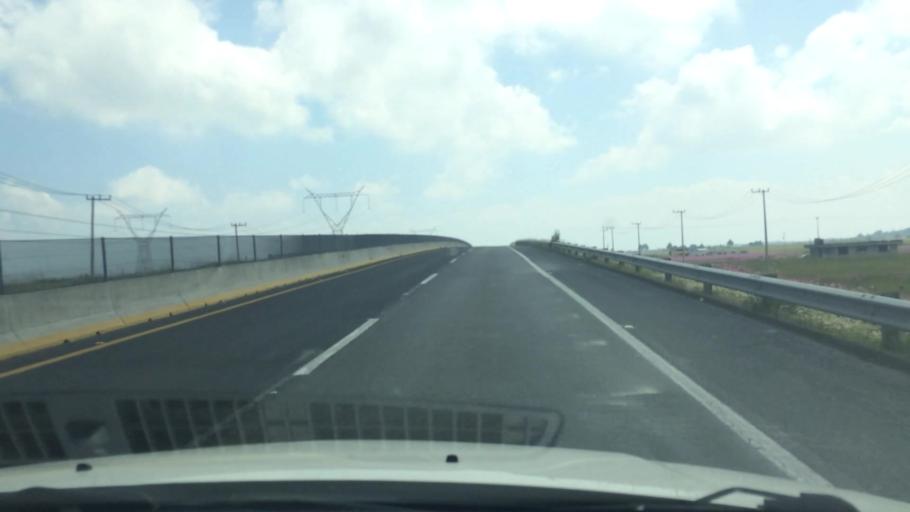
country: MX
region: Mexico
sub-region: Toluca
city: Barrio Bordo Nuevo
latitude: 19.3923
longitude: -99.6713
